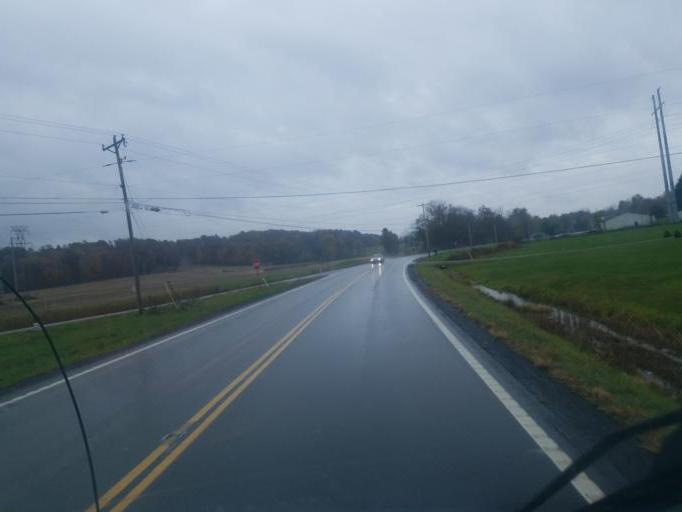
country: US
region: Ohio
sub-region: Muskingum County
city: Frazeysburg
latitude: 40.0816
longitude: -82.1585
